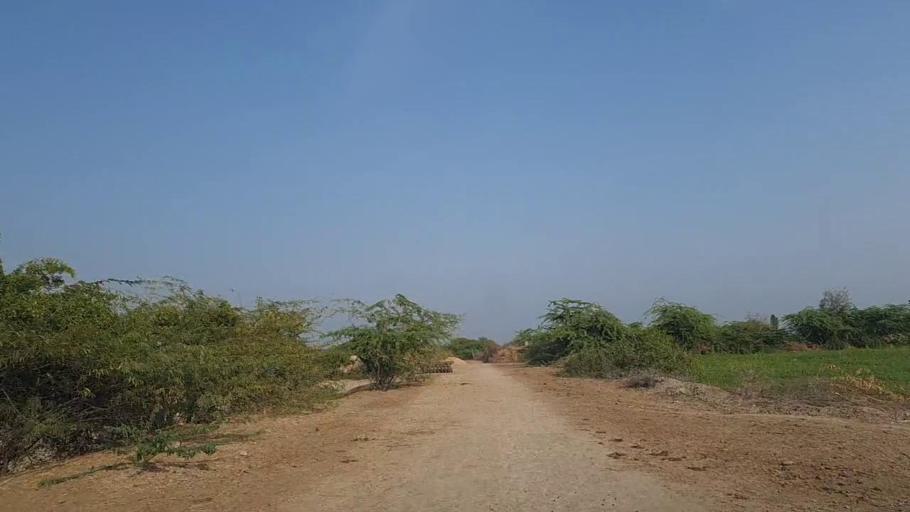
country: PK
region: Sindh
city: Dhoro Naro
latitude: 25.4971
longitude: 69.5003
